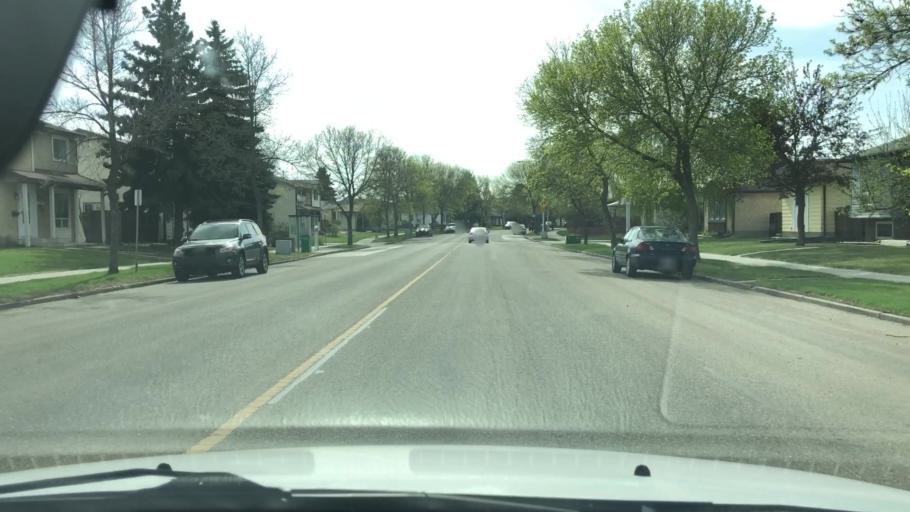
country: CA
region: Alberta
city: Edmonton
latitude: 53.6013
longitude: -113.5242
